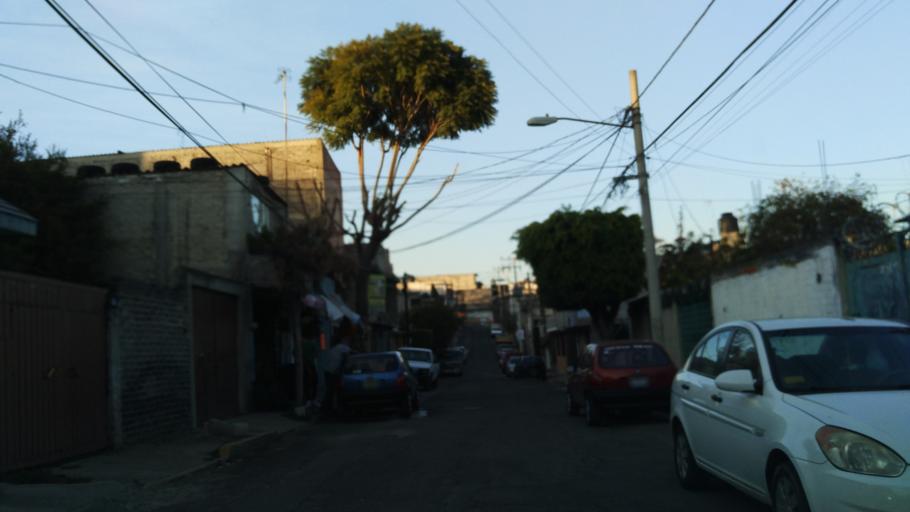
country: MX
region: Mexico City
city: Iztapalapa
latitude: 19.3304
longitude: -99.0863
